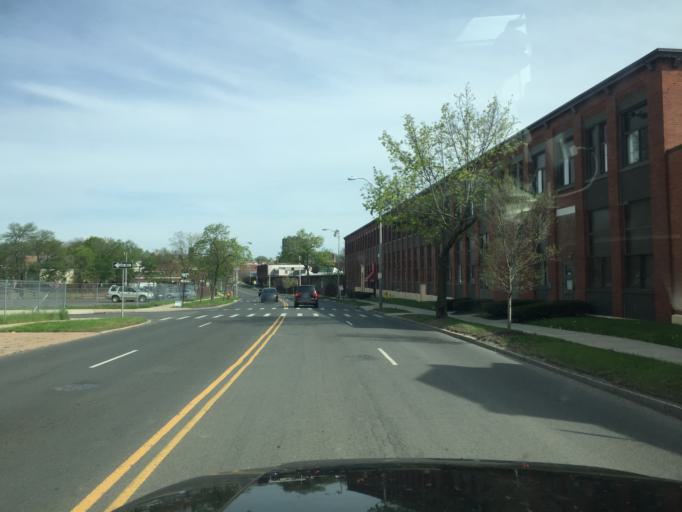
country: US
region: Connecticut
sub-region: Hartford County
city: Hartford
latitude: 41.7808
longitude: -72.7014
